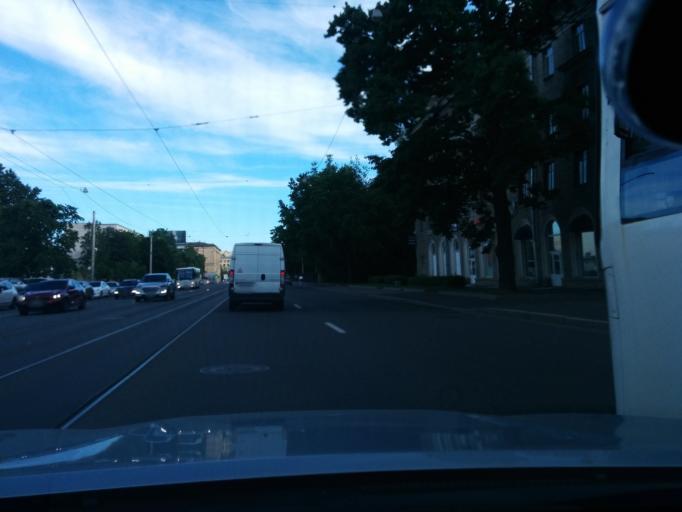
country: RU
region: Leningrad
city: Svetlanovskiy
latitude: 60.0080
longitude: 30.3259
